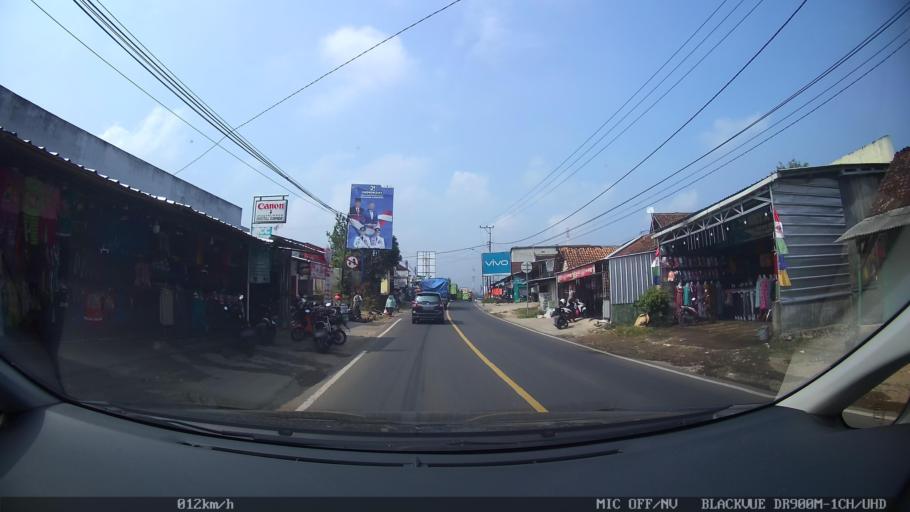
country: ID
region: Lampung
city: Gedongtataan
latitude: -5.3728
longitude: 105.1301
